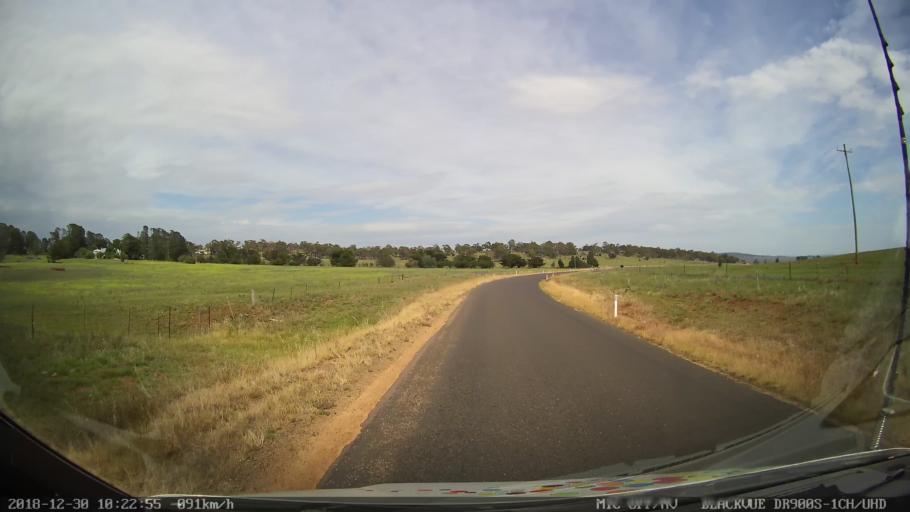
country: AU
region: New South Wales
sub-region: Snowy River
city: Berridale
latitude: -36.5418
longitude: 148.9875
